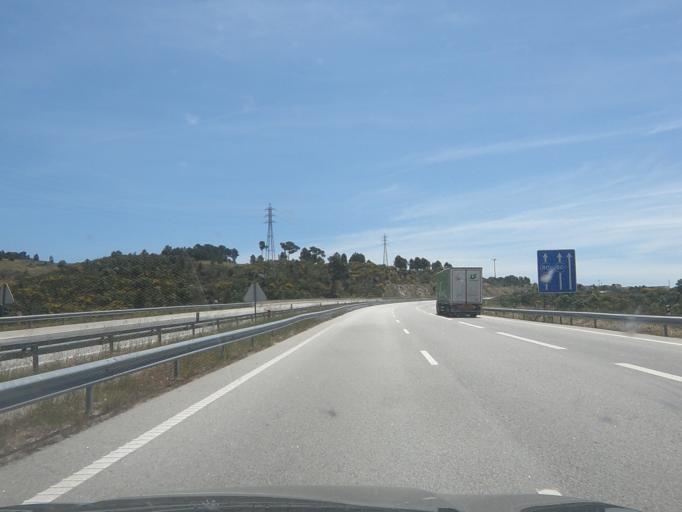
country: PT
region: Guarda
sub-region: Guarda
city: Sequeira
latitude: 40.5676
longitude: -7.2449
